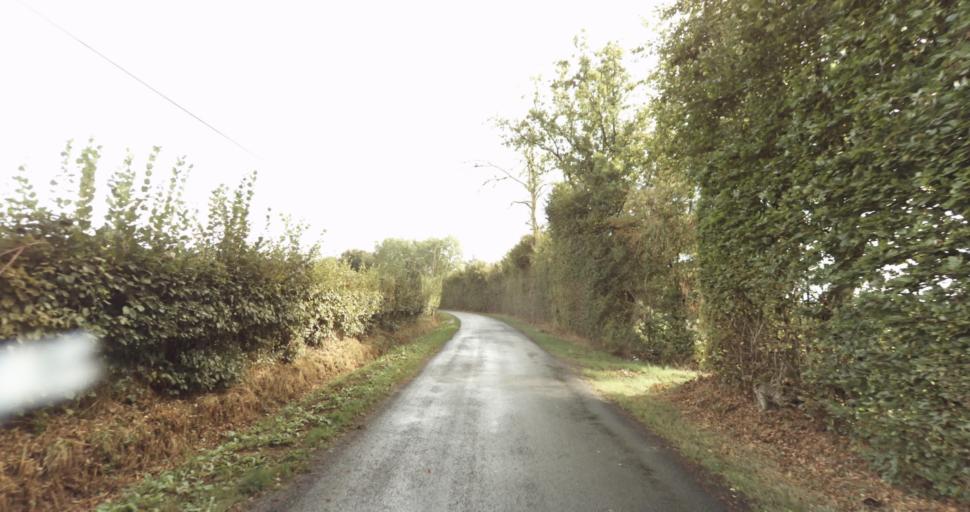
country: FR
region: Lower Normandy
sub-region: Departement de l'Orne
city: Sainte-Gauburge-Sainte-Colombe
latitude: 48.6847
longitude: 0.3852
